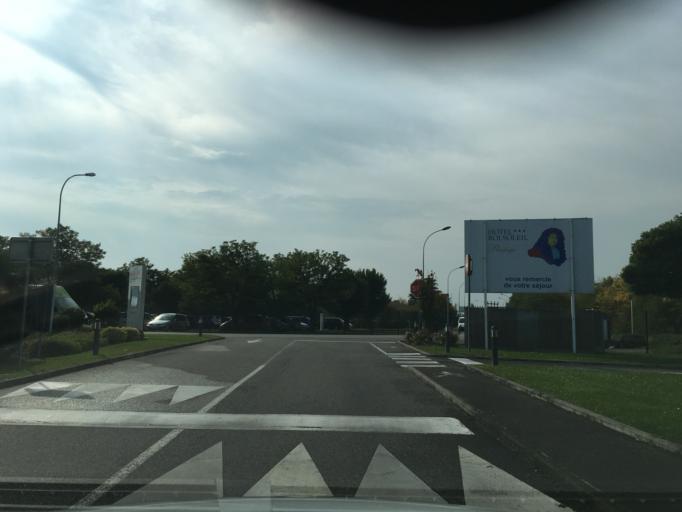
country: FR
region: Alsace
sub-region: Departement du Haut-Rhin
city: Houssen
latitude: 48.1118
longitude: 7.3648
